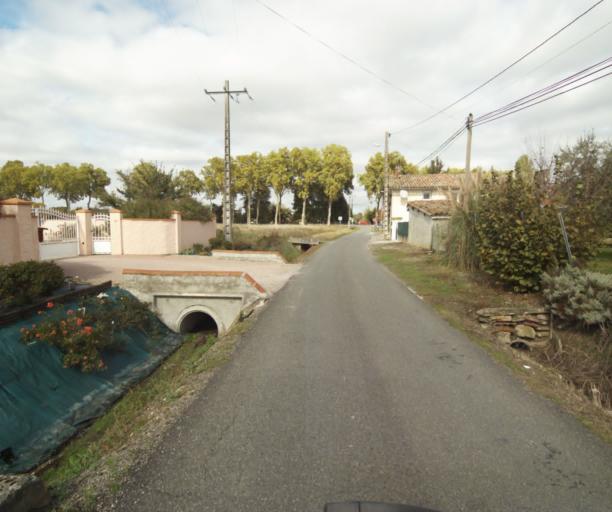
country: FR
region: Midi-Pyrenees
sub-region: Departement du Tarn-et-Garonne
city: Montech
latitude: 43.9546
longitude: 1.2235
